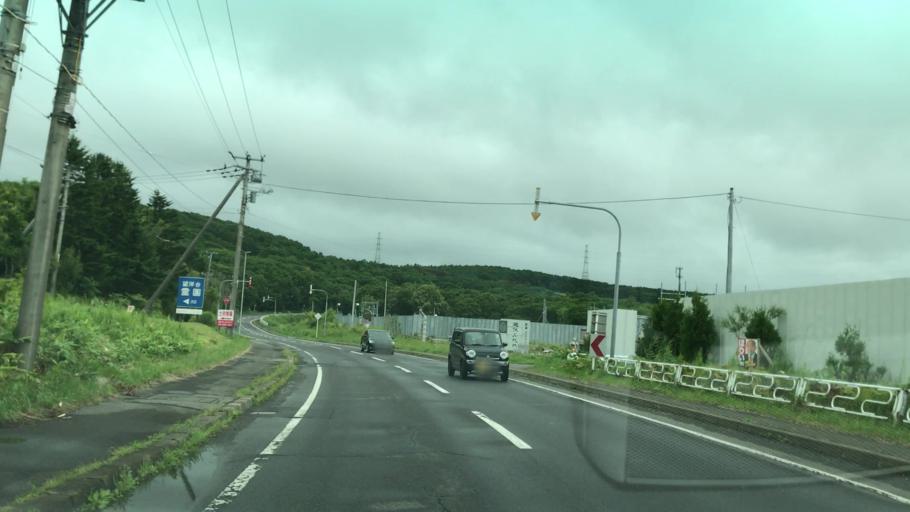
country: JP
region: Hokkaido
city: Muroran
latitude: 42.3916
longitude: 141.0021
